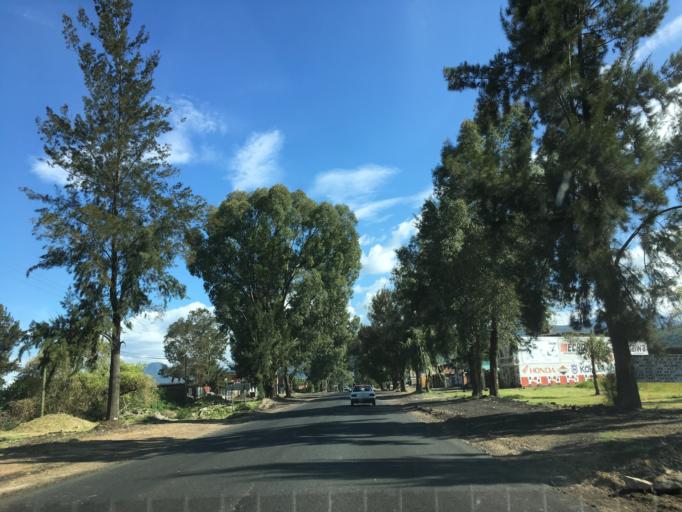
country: MX
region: Michoacan
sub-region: Zacapu
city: Naranja de Tapia
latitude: 19.7940
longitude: -101.7748
